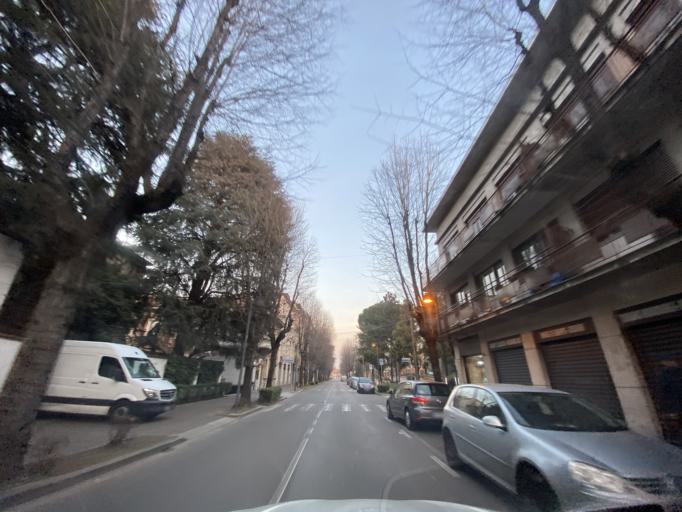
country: IT
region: Lombardy
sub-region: Provincia di Monza e Brianza
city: Bovisio-Masciago
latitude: 45.5969
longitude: 9.1486
